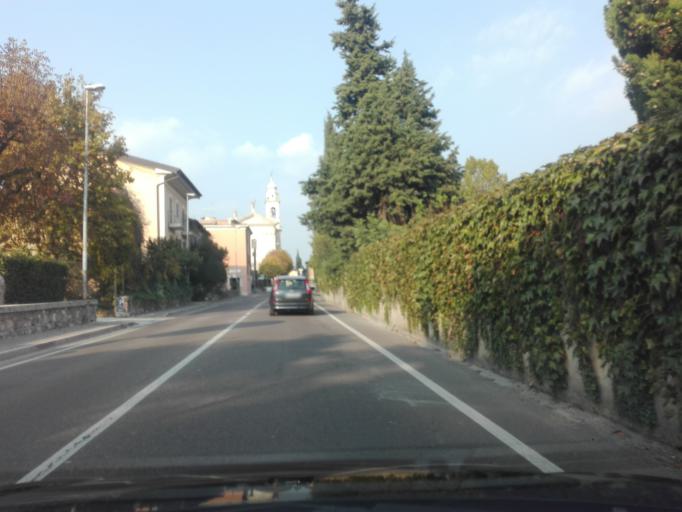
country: IT
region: Veneto
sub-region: Provincia di Verona
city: Cola
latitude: 45.4652
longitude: 10.7202
